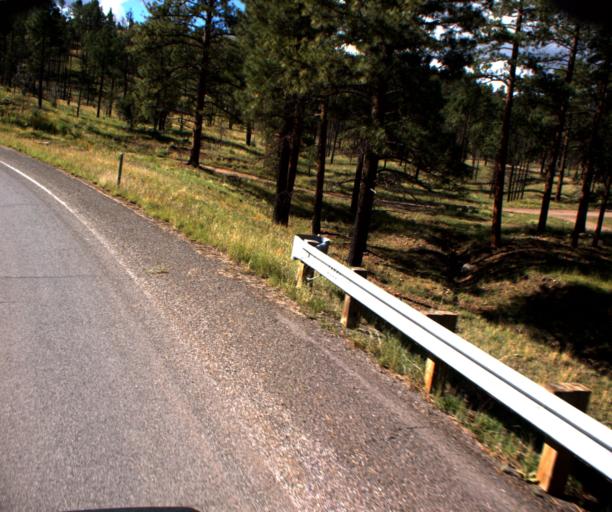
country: US
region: Arizona
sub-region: Apache County
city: Eagar
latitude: 34.0752
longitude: -109.3537
